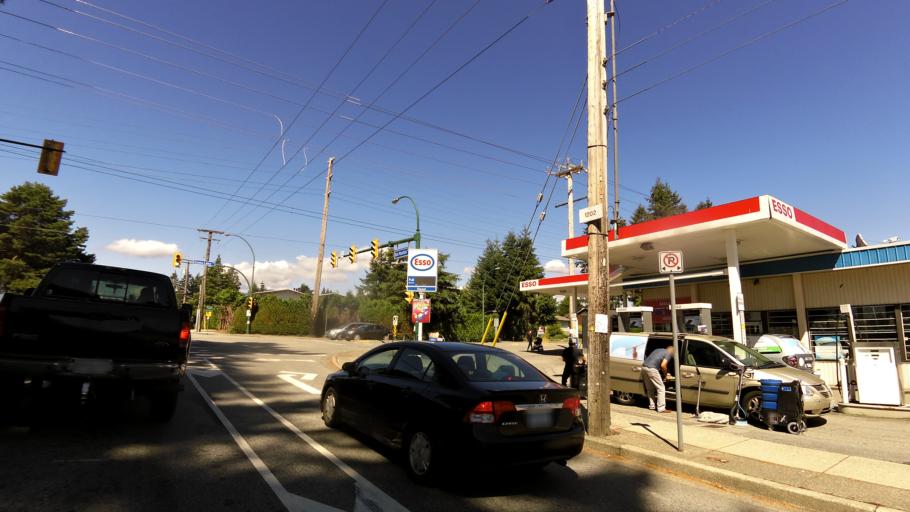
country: CA
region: British Columbia
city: Port Moody
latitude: 49.2633
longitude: -122.8687
